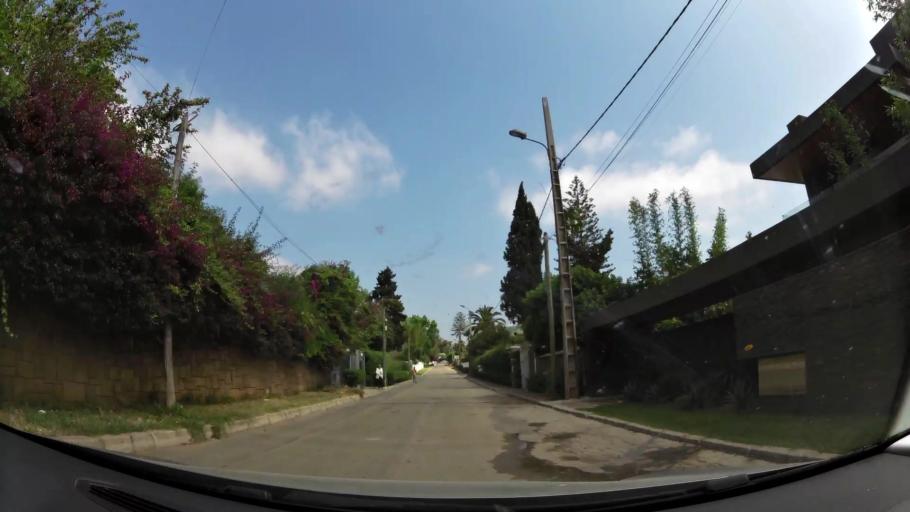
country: MA
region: Rabat-Sale-Zemmour-Zaer
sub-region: Rabat
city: Rabat
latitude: 33.9807
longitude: -6.8383
